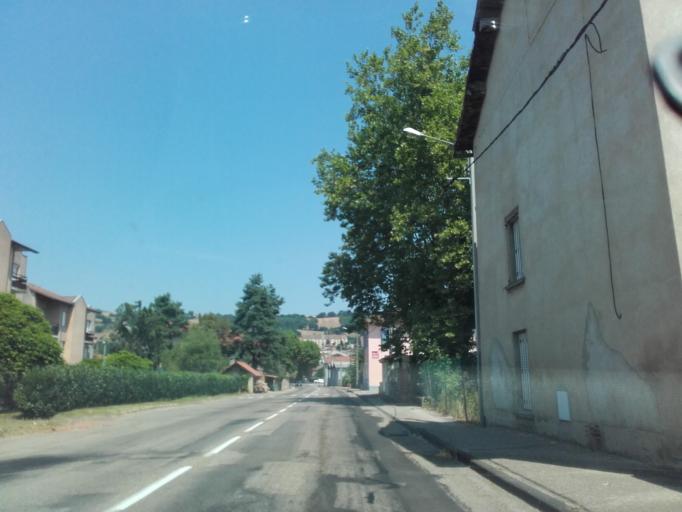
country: FR
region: Rhone-Alpes
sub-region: Departement de l'Isere
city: La Cote-Saint-Andre
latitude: 45.3856
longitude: 5.2627
